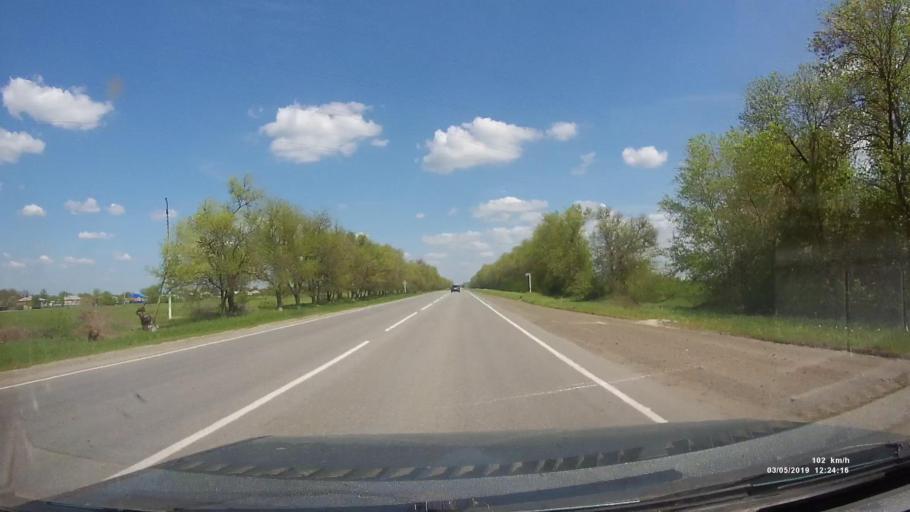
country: RU
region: Rostov
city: Semikarakorsk
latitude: 47.4182
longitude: 40.6964
